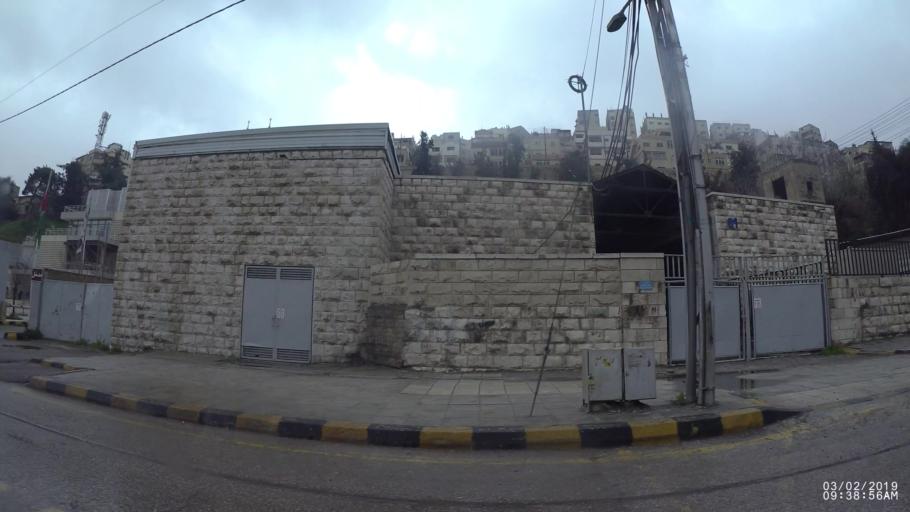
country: JO
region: Amman
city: Amman
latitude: 31.9446
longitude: 35.9203
